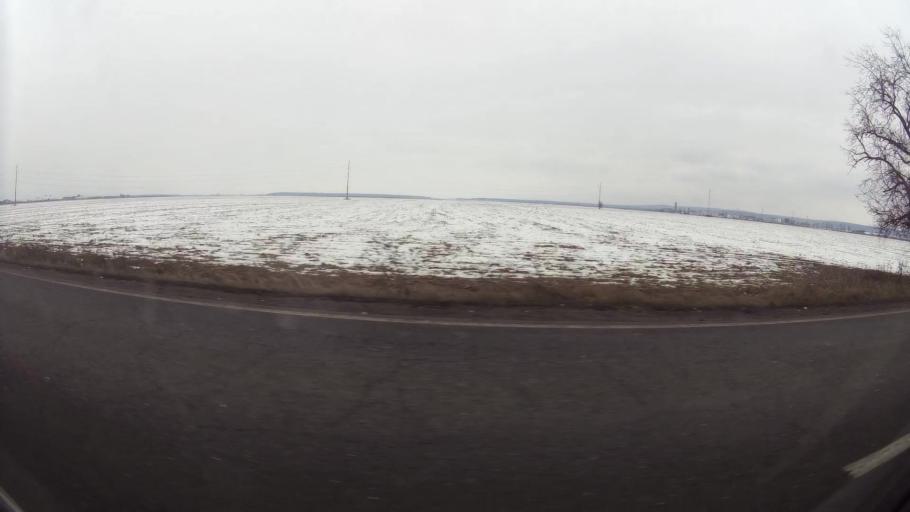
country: RO
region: Prahova
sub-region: Comuna Paulesti
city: Paulesti
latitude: 44.9721
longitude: 25.9854
